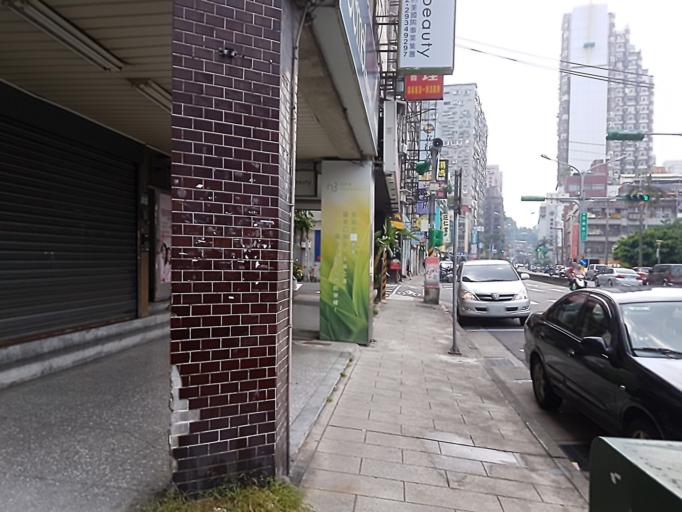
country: TW
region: Taipei
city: Taipei
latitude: 24.9940
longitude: 121.5447
